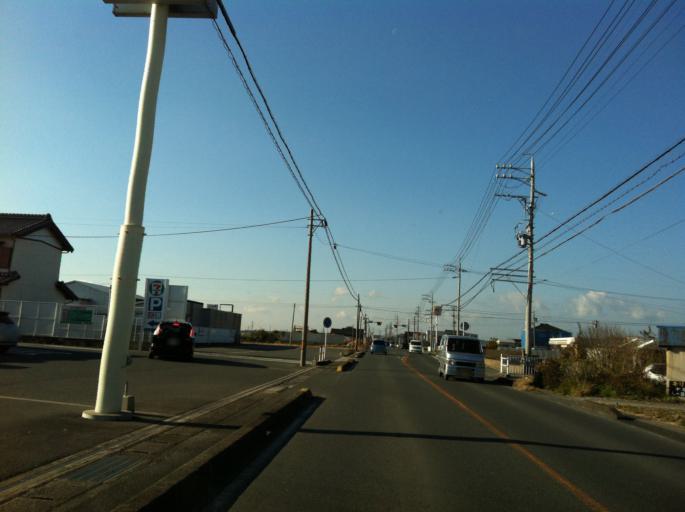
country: JP
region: Aichi
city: Tahara
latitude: 34.6892
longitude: 137.3247
